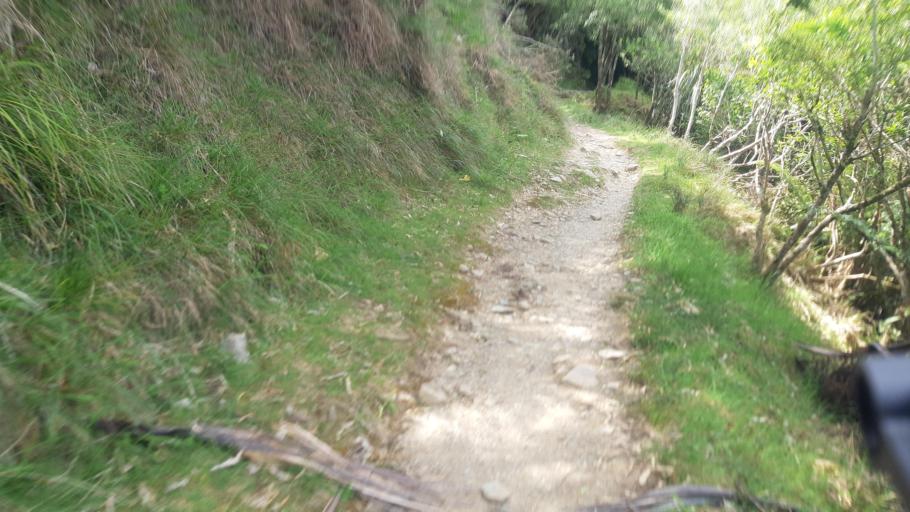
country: NZ
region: Marlborough
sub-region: Marlborough District
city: Picton
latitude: -41.2499
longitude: 173.9614
